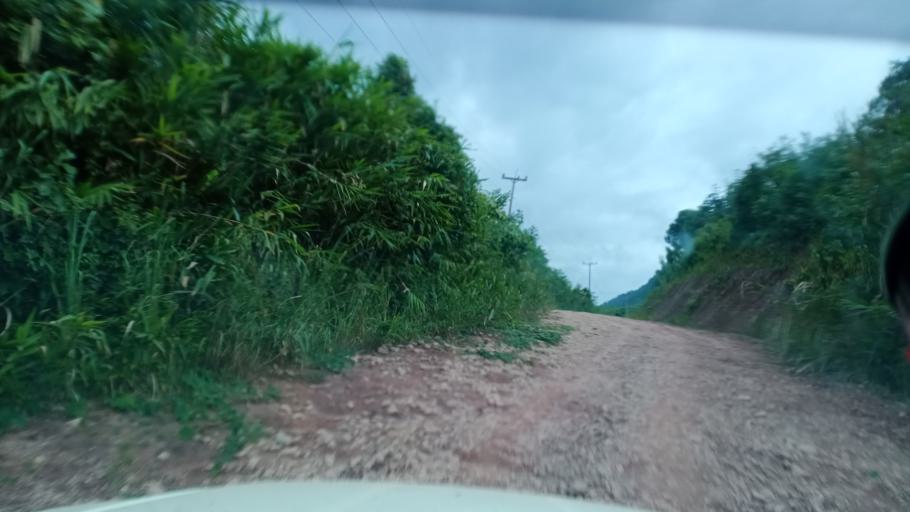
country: TH
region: Changwat Bueng Kan
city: Pak Khat
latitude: 18.7262
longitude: 103.2663
